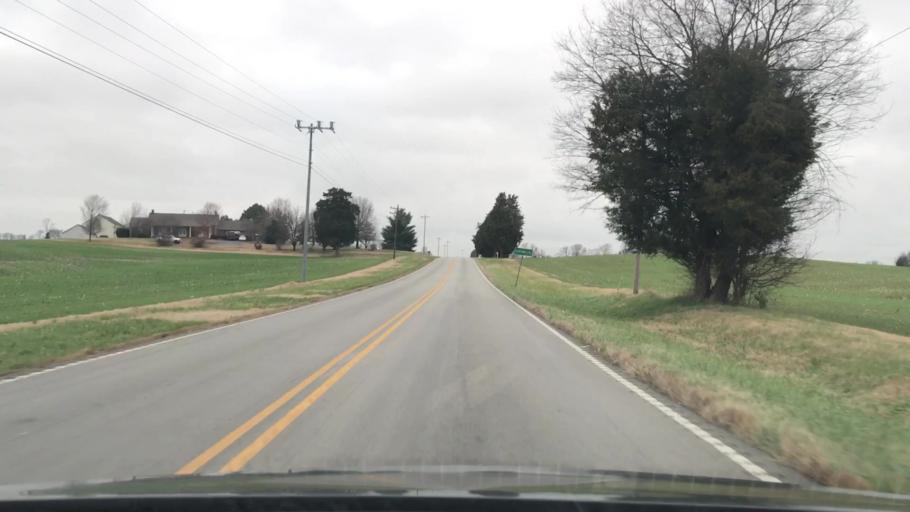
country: US
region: Kentucky
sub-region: Todd County
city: Guthrie
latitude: 36.6496
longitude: -87.1999
